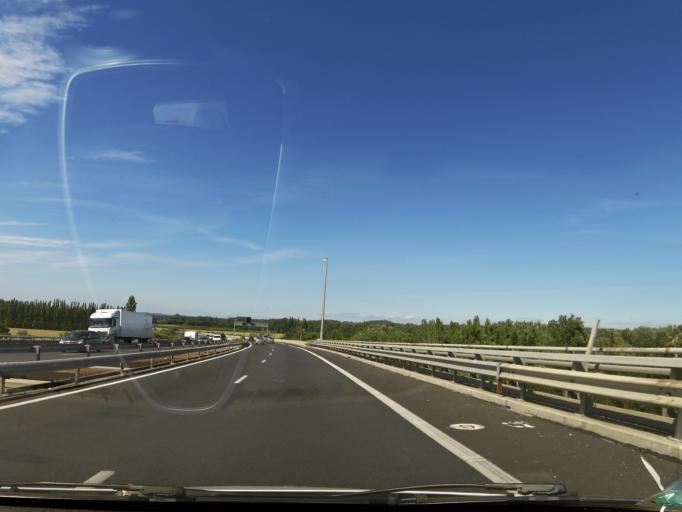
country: FR
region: Languedoc-Roussillon
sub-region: Departement du Gard
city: Roquemaure
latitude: 44.0550
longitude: 4.7677
